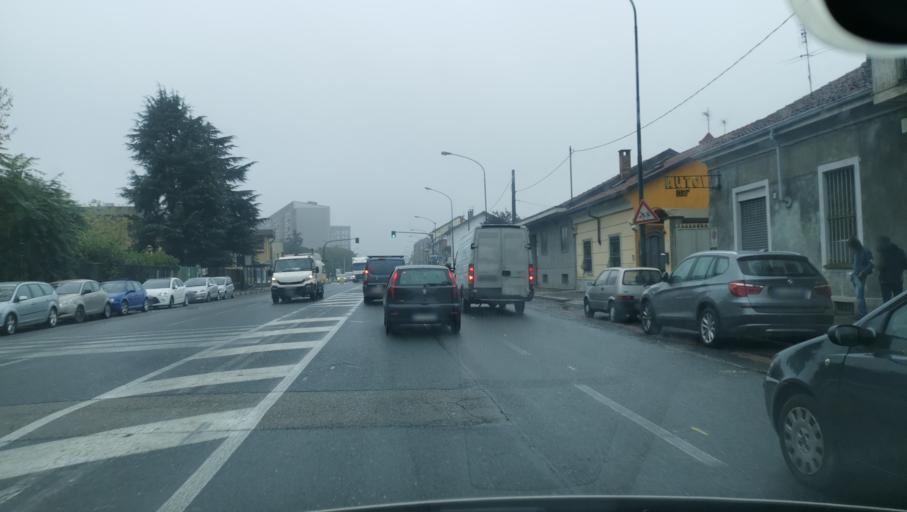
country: IT
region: Piedmont
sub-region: Provincia di Torino
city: Turin
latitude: 45.1071
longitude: 7.6935
